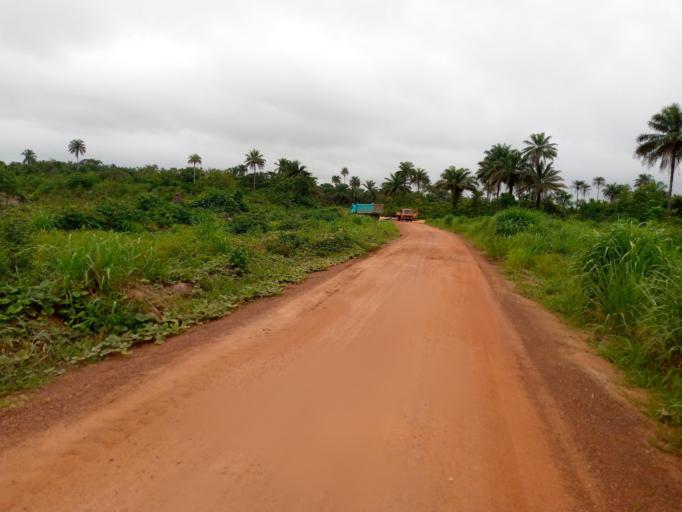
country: SL
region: Southern Province
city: Sumbuya
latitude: 7.5779
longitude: -12.0851
